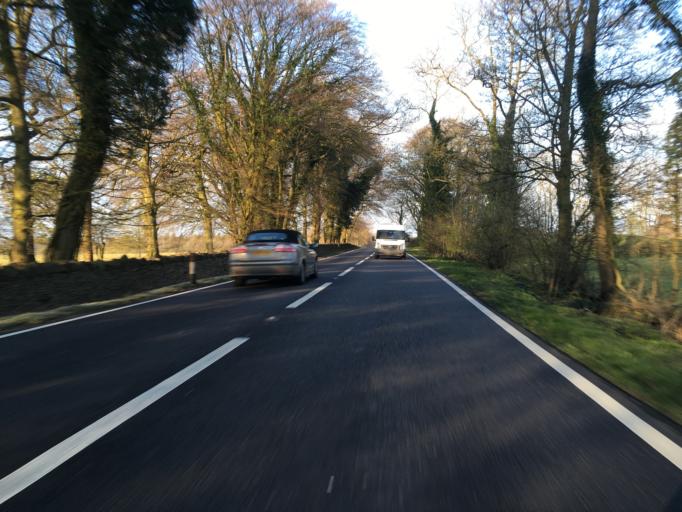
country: GB
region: England
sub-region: Gloucestershire
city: Charlton Kings
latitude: 51.8633
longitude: -2.0261
